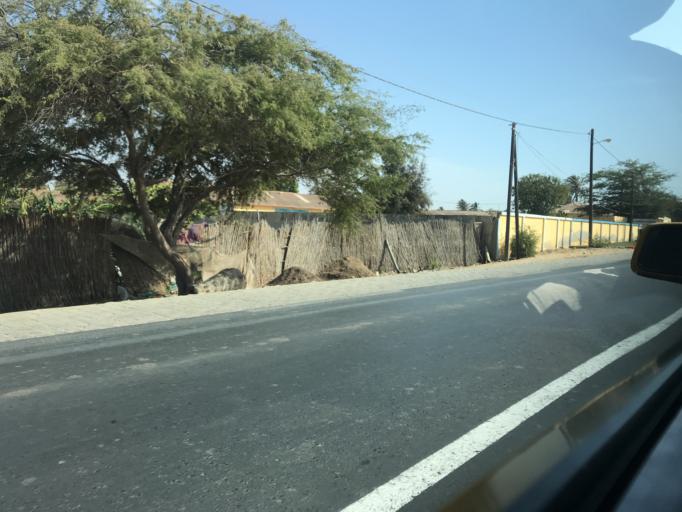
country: SN
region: Saint-Louis
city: Saint-Louis
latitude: 16.0291
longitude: -16.4743
